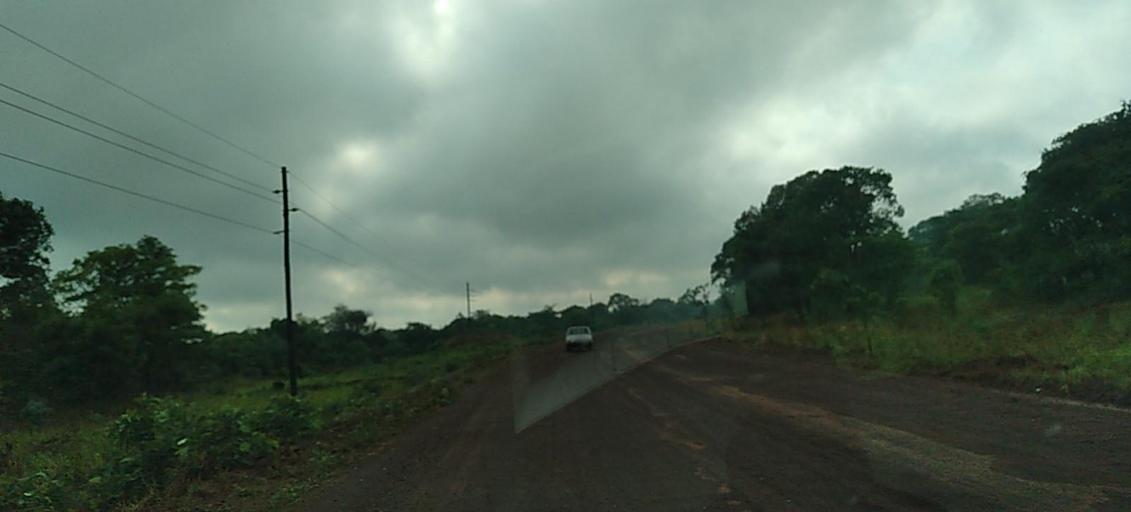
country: ZM
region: North-Western
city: Mwinilunga
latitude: -11.7254
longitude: 24.5743
